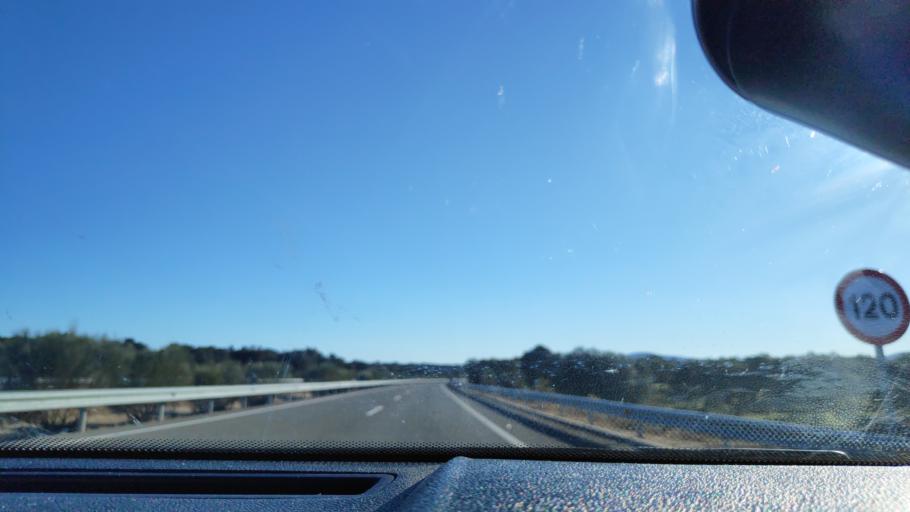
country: ES
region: Andalusia
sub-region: Provincia de Huelva
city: Cala
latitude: 37.9895
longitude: -6.2329
